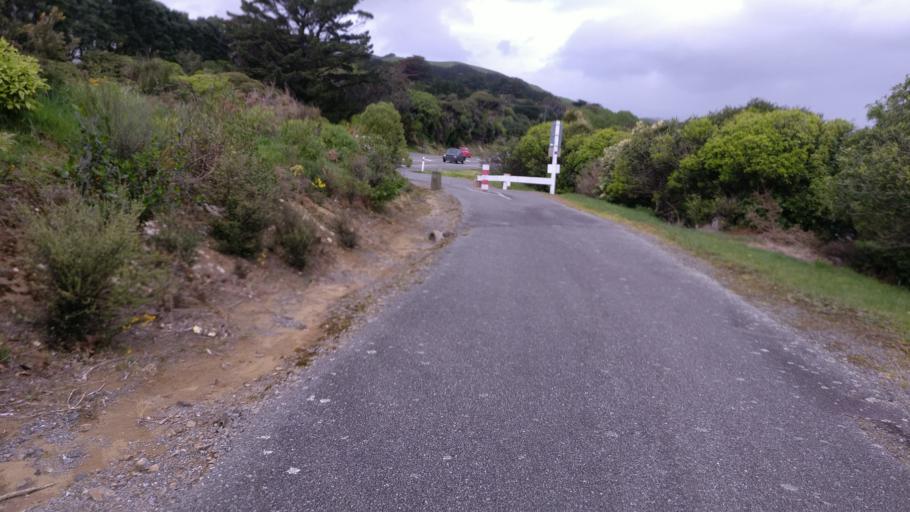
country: NZ
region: Wellington
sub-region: Porirua City
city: Porirua
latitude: -41.0421
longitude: 174.8839
